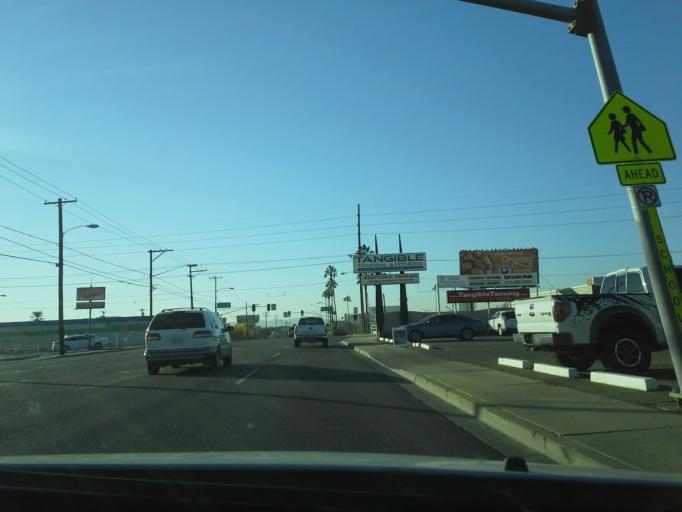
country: US
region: Arizona
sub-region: Maricopa County
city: Phoenix
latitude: 33.5033
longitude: -112.0651
